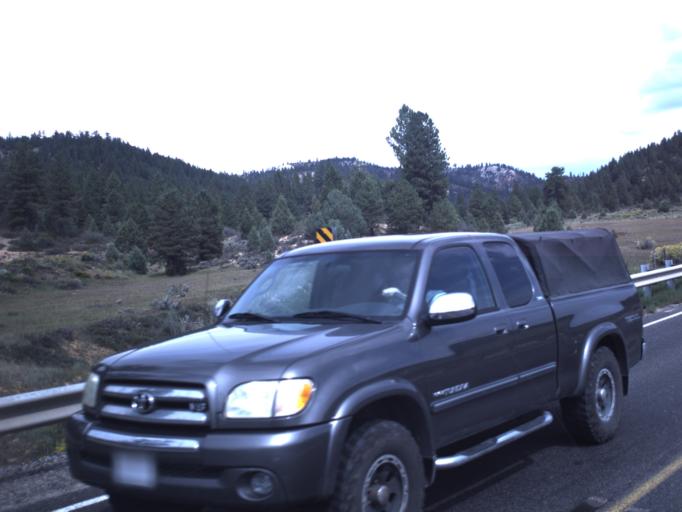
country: US
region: Utah
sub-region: Garfield County
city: Panguitch
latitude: 37.4427
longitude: -112.5375
